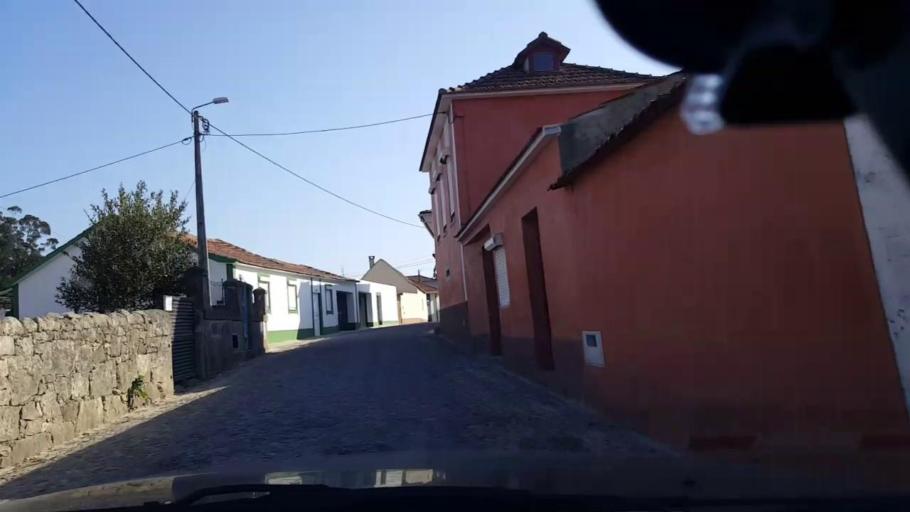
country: PT
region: Porto
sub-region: Vila do Conde
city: Arvore
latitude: 41.3550
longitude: -8.7218
